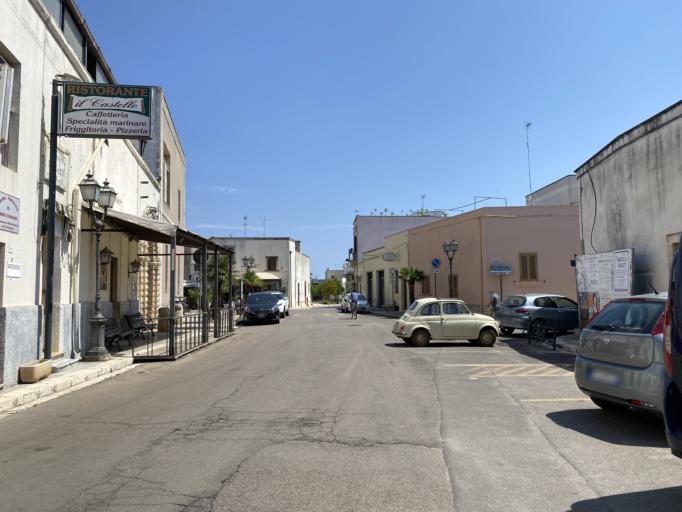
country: IT
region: Apulia
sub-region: Provincia di Lecce
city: Giuggianello
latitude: 40.0951
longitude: 18.3682
